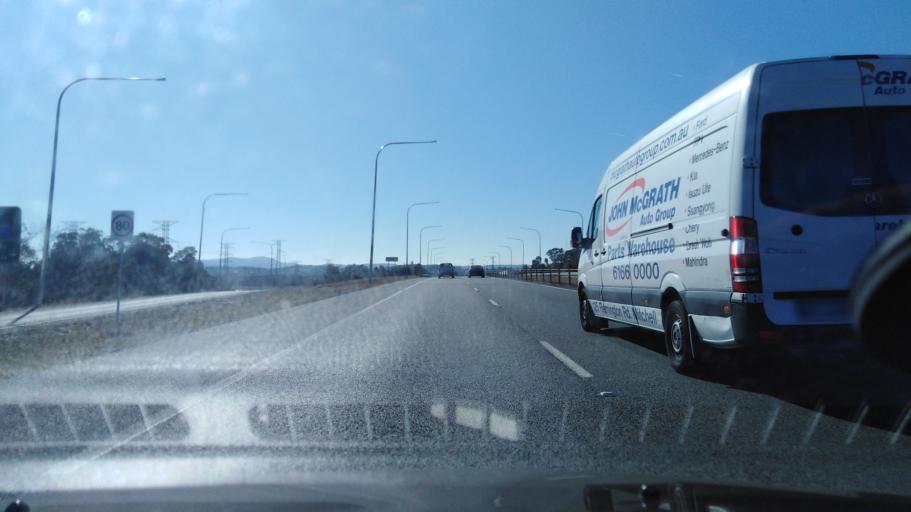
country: AU
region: Australian Capital Territory
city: Kaleen
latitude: -35.2457
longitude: 149.1103
